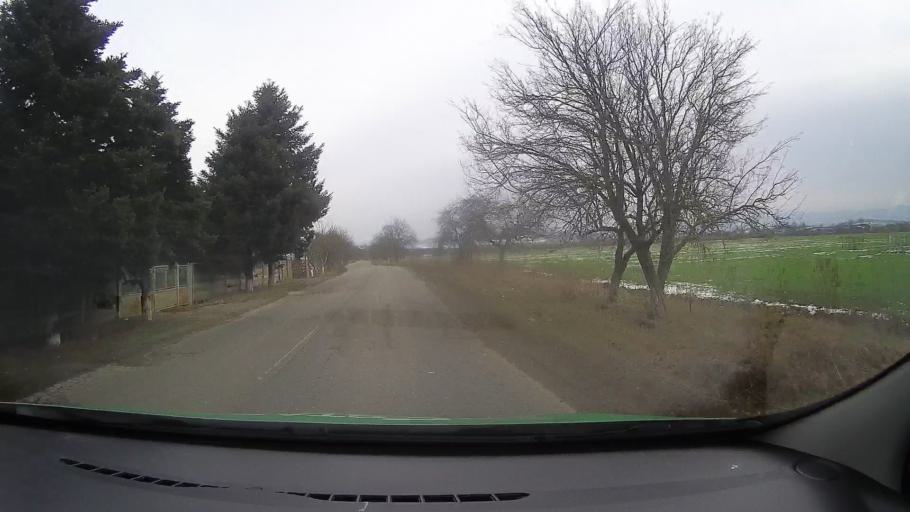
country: RO
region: Hunedoara
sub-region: Comuna Romos
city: Romos
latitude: 45.8832
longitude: 23.2512
